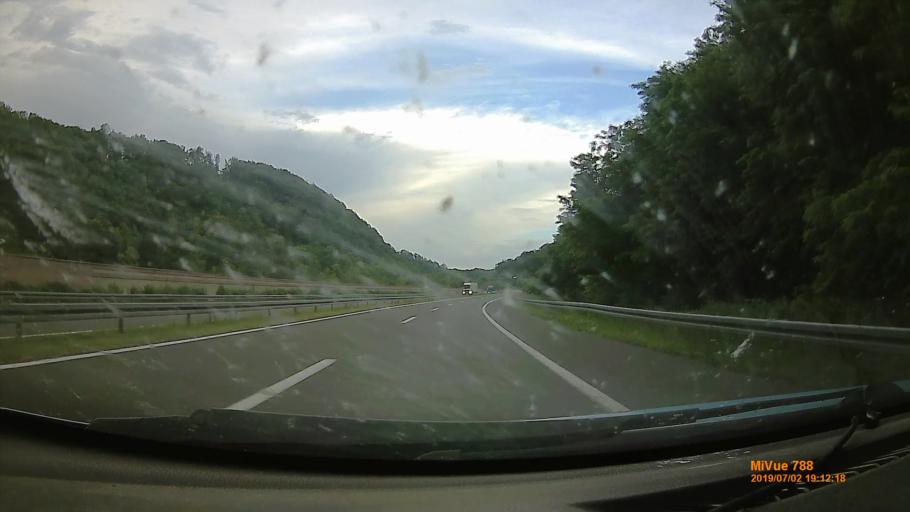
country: HR
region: Varazdinska
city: Remetinec
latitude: 46.1205
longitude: 16.2969
